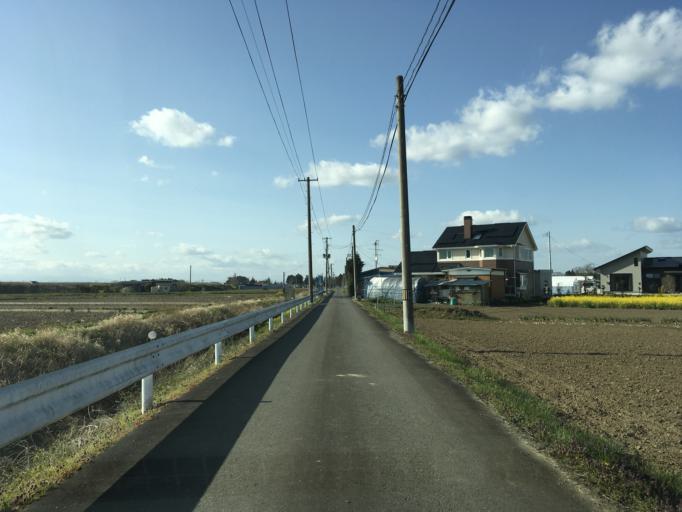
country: JP
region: Miyagi
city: Wakuya
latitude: 38.6615
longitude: 141.2174
